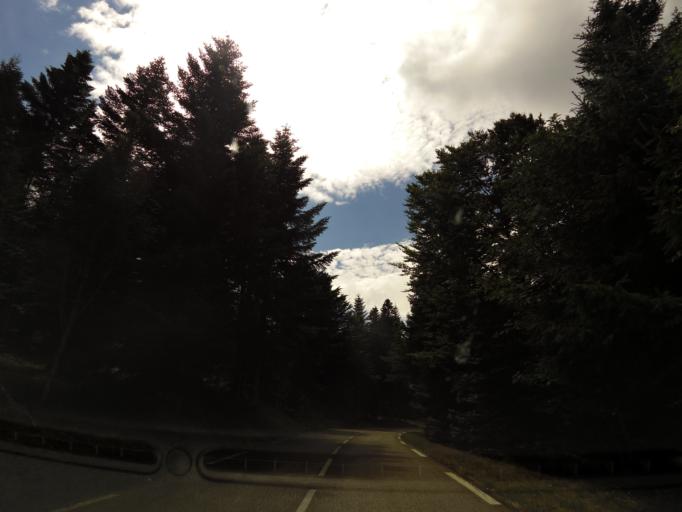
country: FR
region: Languedoc-Roussillon
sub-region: Departement de la Lozere
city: Meyrueis
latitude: 44.1027
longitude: 3.5209
